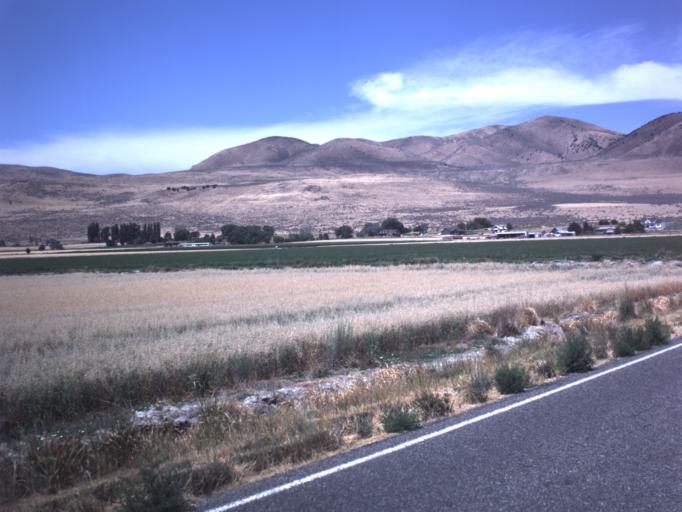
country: US
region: Utah
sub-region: Box Elder County
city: Tremonton
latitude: 41.6449
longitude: -112.3142
